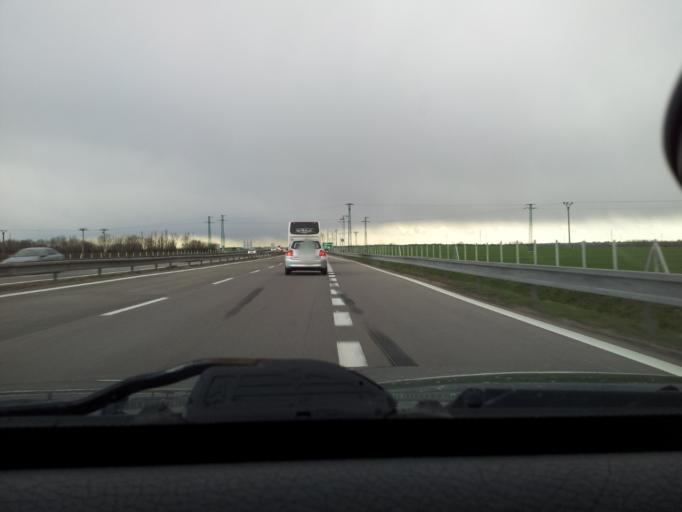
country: SK
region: Trnavsky
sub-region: Okres Trnava
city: Trnava
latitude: 48.3333
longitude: 17.6322
